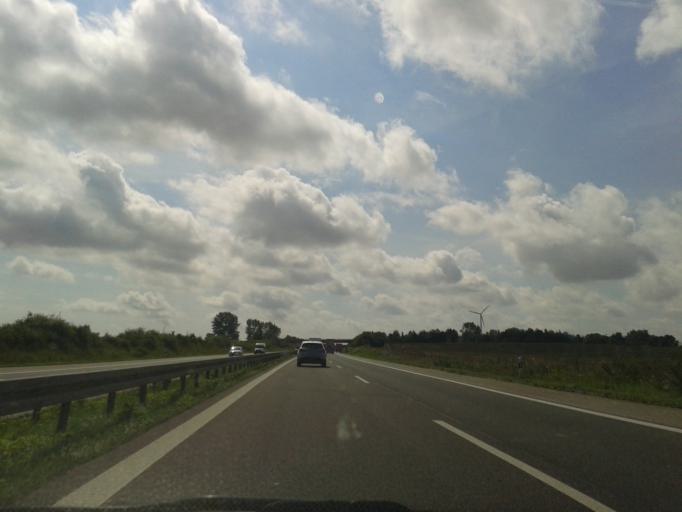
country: DE
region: Brandenburg
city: Grunow
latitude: 53.3340
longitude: 13.9849
